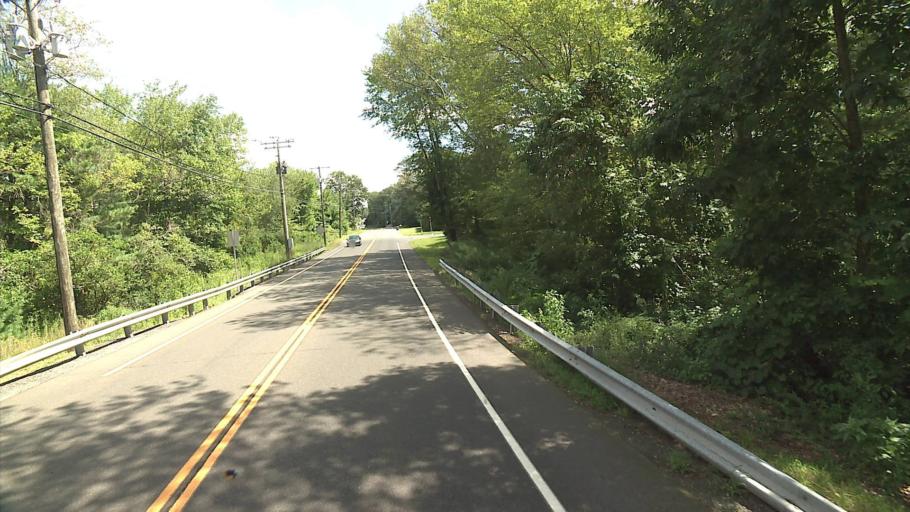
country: US
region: Connecticut
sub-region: New London County
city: Niantic
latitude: 41.3652
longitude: -72.2341
